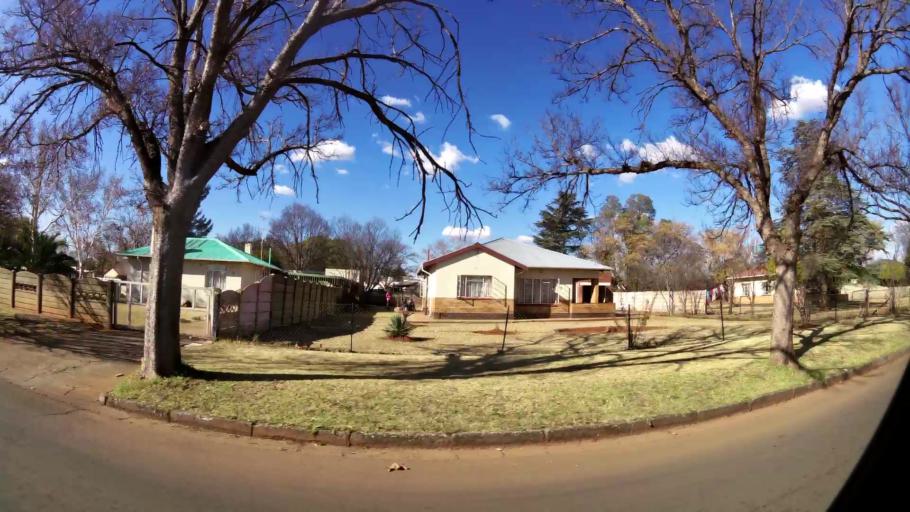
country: ZA
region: Gauteng
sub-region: West Rand District Municipality
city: Carletonville
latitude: -26.3679
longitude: 27.3947
